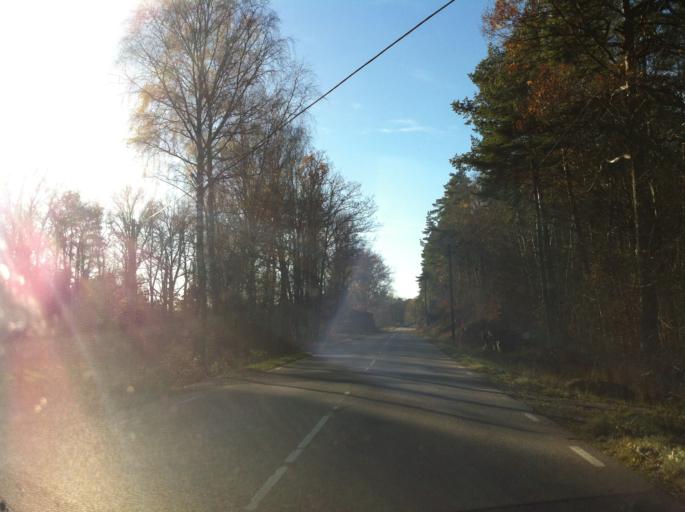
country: SE
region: Blekinge
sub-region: Karlshamns Kommun
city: Karlshamn
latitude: 56.1989
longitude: 14.9597
